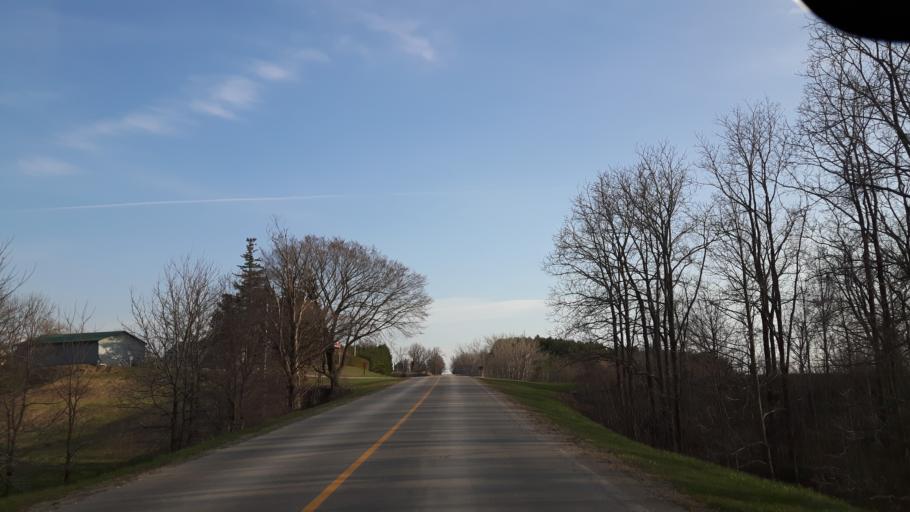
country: CA
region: Ontario
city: Goderich
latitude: 43.6734
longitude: -81.6644
